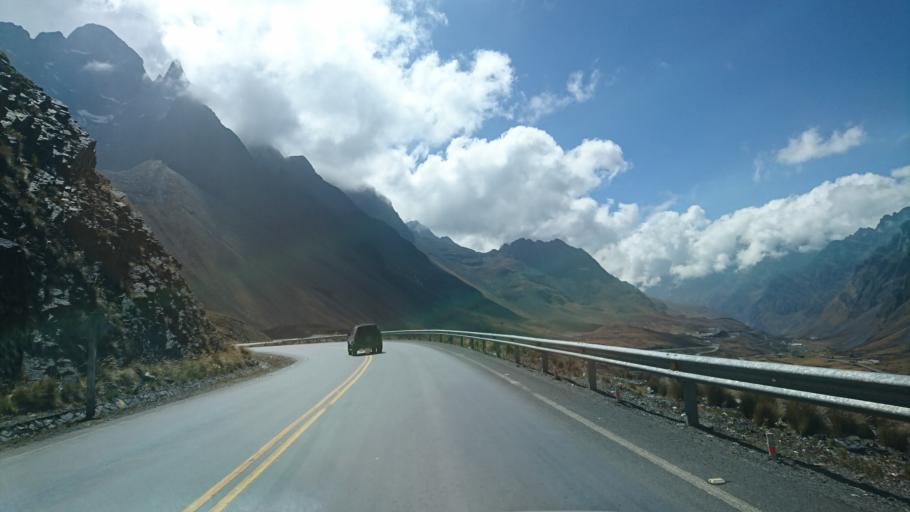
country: BO
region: La Paz
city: La Paz
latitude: -16.3204
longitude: -68.0269
